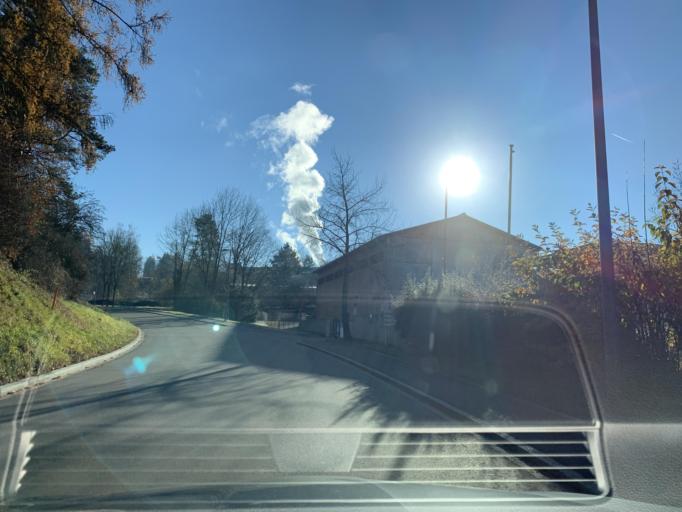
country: DE
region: Bavaria
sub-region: Upper Palatinate
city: Neunburg vorm Wald
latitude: 49.3434
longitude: 12.3965
